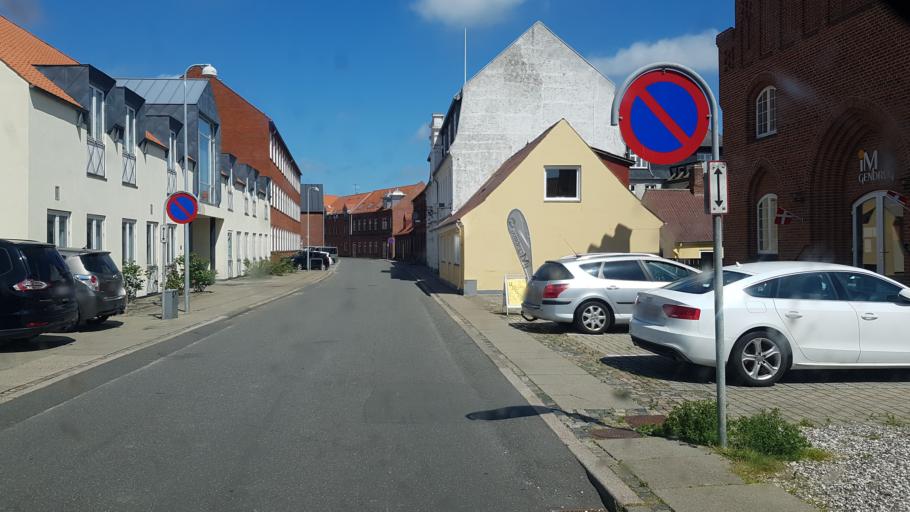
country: DK
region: Central Jutland
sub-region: Lemvig Kommune
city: Lemvig
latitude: 56.5482
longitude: 8.3105
